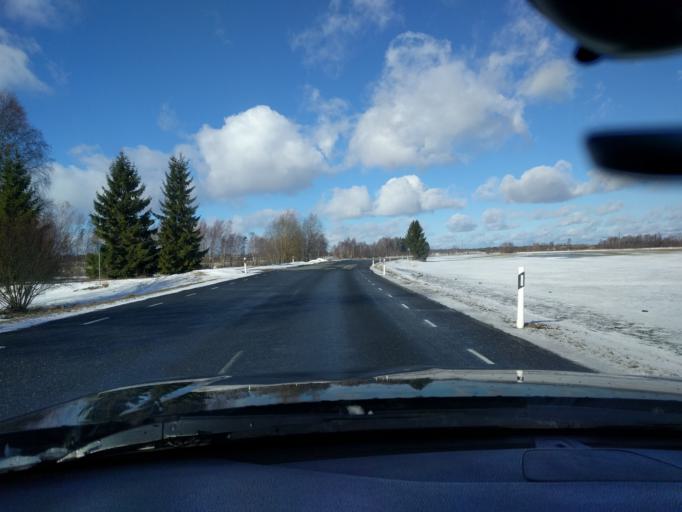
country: EE
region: Harju
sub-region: Anija vald
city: Kehra
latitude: 59.2433
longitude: 25.3569
